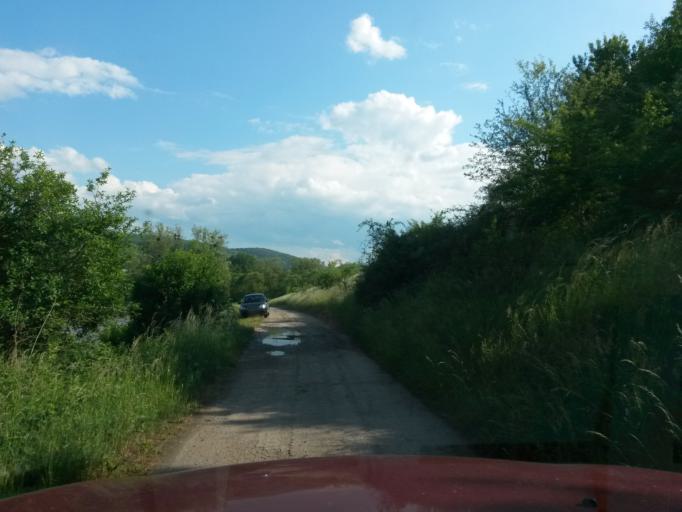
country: SK
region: Kosicky
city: Roznava
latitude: 48.5891
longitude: 20.6441
